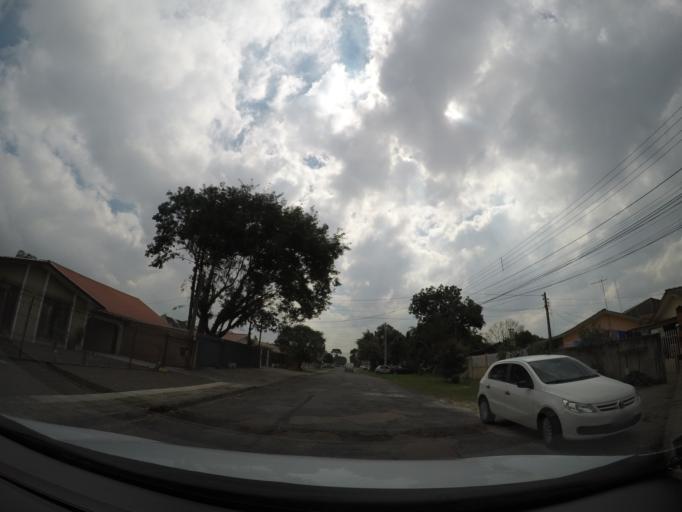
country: BR
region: Parana
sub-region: Sao Jose Dos Pinhais
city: Sao Jose dos Pinhais
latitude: -25.5003
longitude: -49.2478
